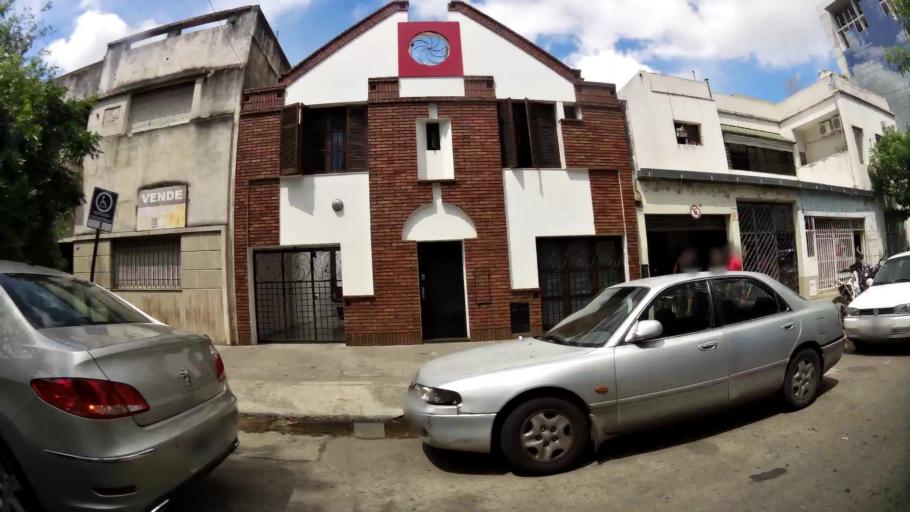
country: AR
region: Santa Fe
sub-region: Departamento de Rosario
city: Rosario
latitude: -32.9602
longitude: -60.6384
